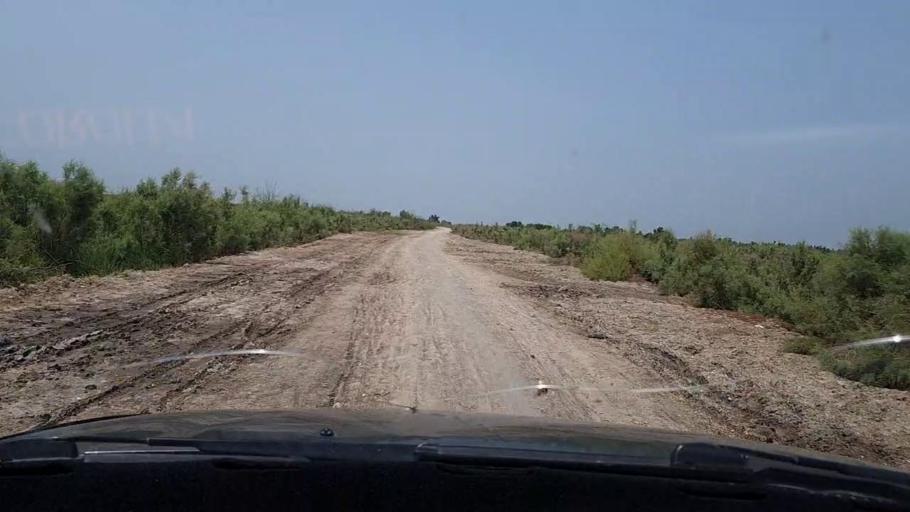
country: PK
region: Sindh
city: Adilpur
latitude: 27.8985
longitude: 69.2362
